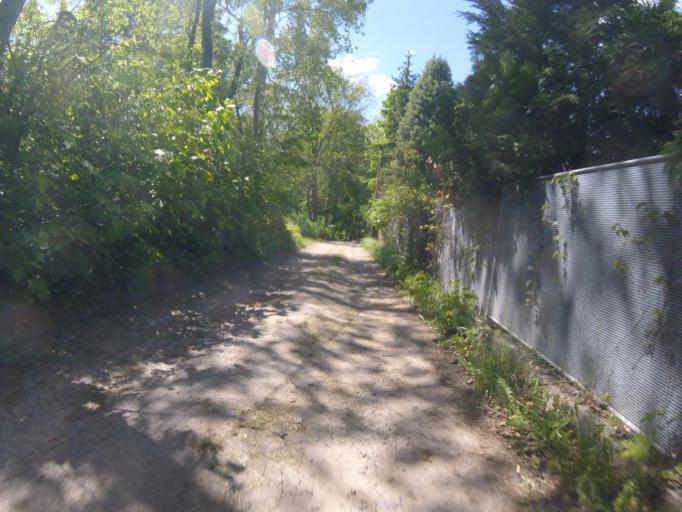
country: DE
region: Brandenburg
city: Teupitz
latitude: 52.1369
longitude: 13.6279
